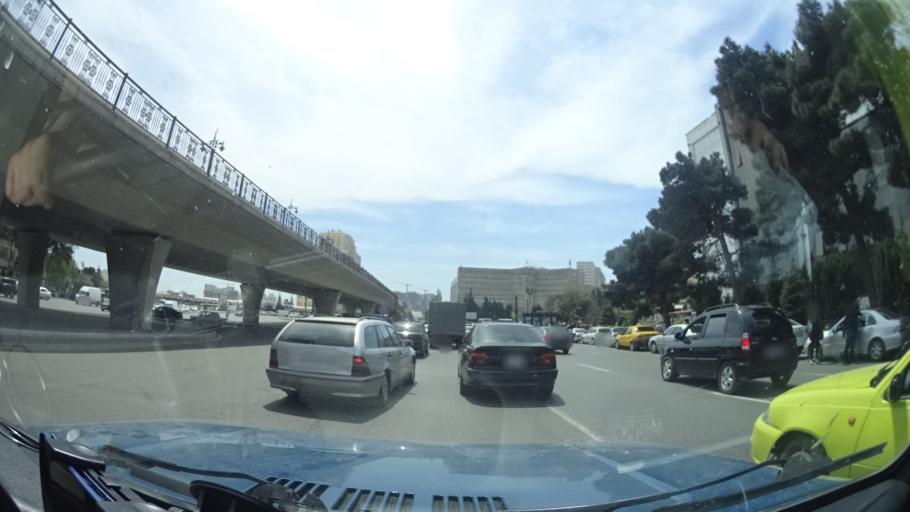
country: AZ
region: Baki
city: Khodzhi-Gasan
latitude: 40.4051
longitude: 49.8069
